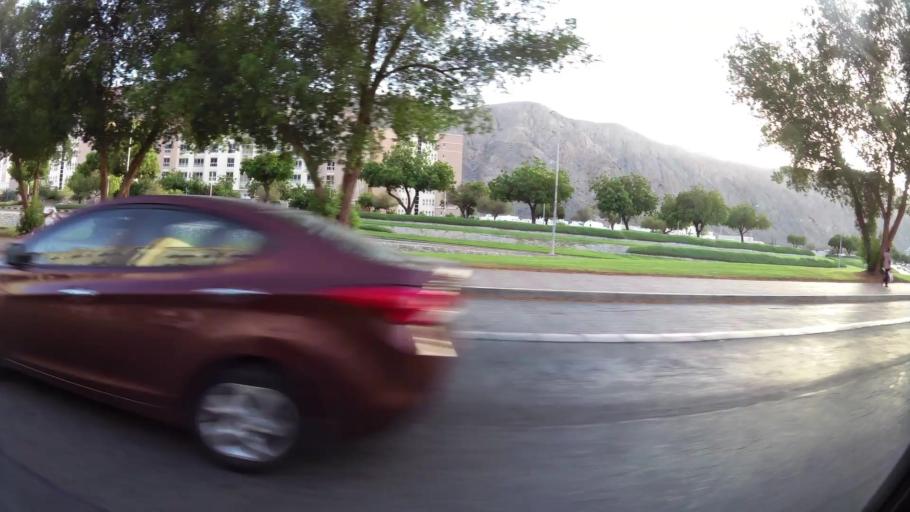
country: OM
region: Muhafazat Masqat
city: Muscat
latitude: 23.5704
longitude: 58.5723
